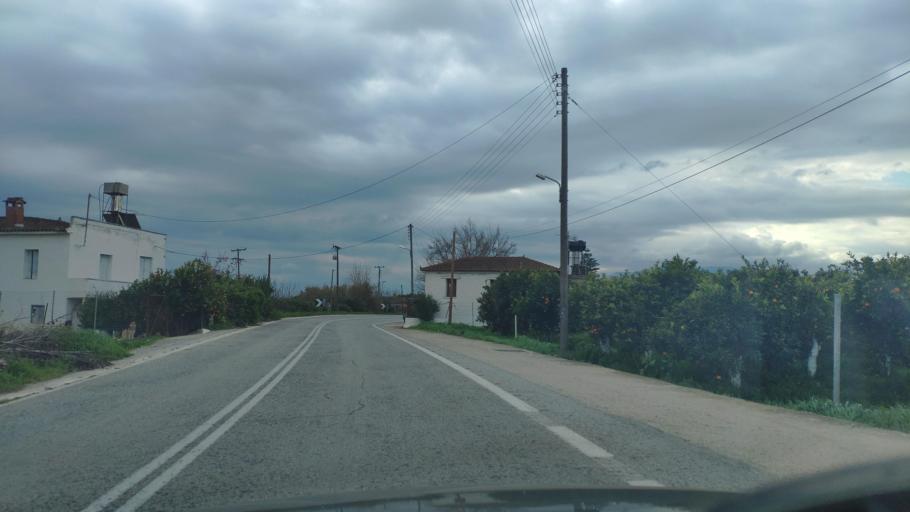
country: GR
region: Peloponnese
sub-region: Nomos Argolidos
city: Nea Kios
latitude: 37.5858
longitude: 22.7094
